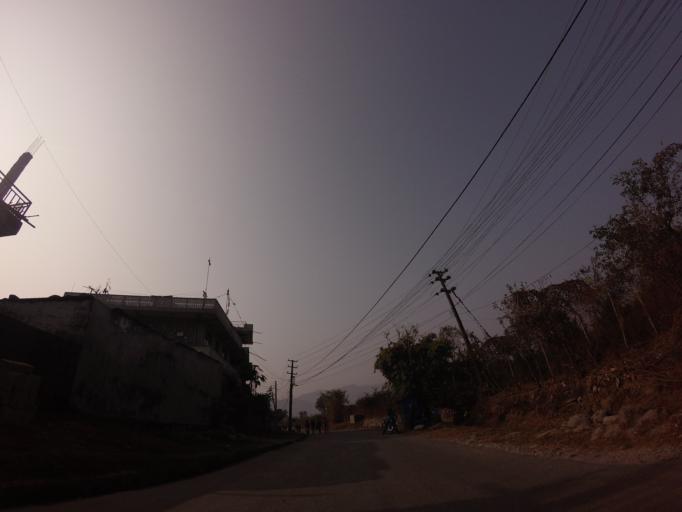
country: NP
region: Western Region
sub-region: Gandaki Zone
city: Pokhara
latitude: 28.1997
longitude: 83.9838
